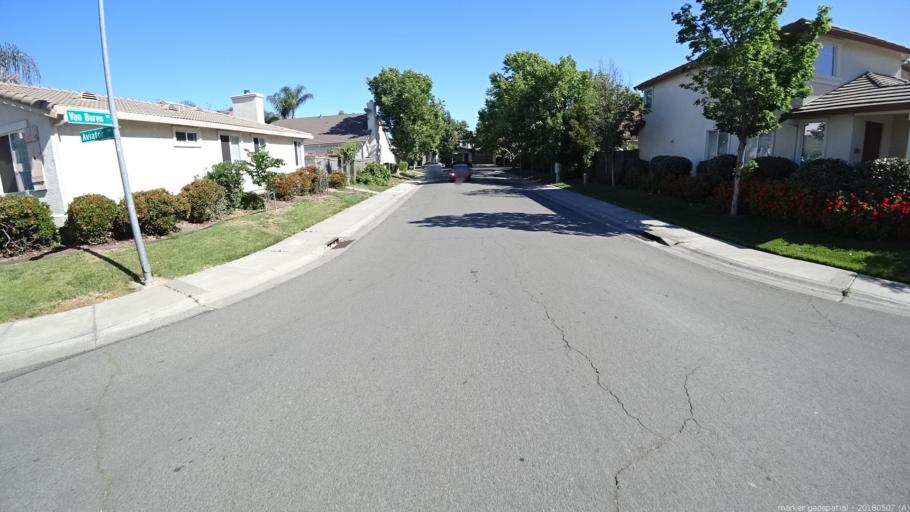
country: US
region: California
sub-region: Sacramento County
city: Rio Linda
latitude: 38.6590
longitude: -121.5049
